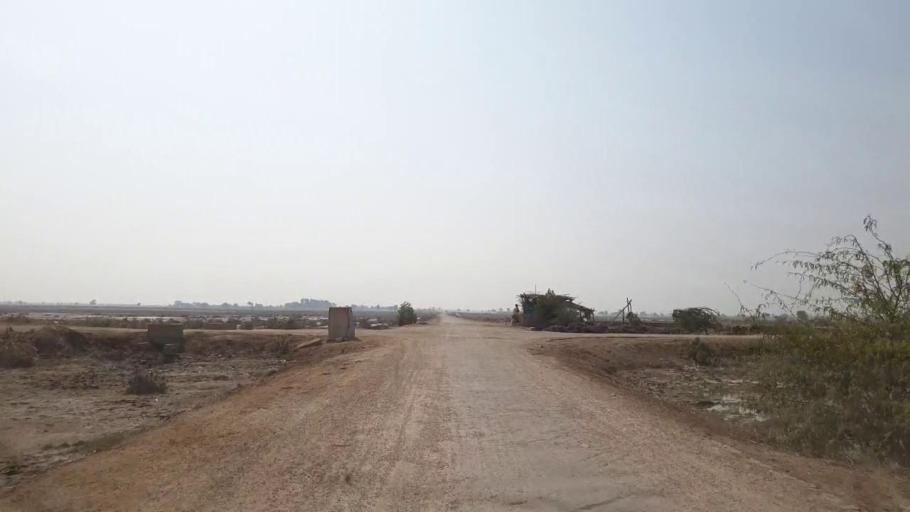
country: PK
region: Sindh
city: Mirpur Khas
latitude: 25.5829
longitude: 69.0255
